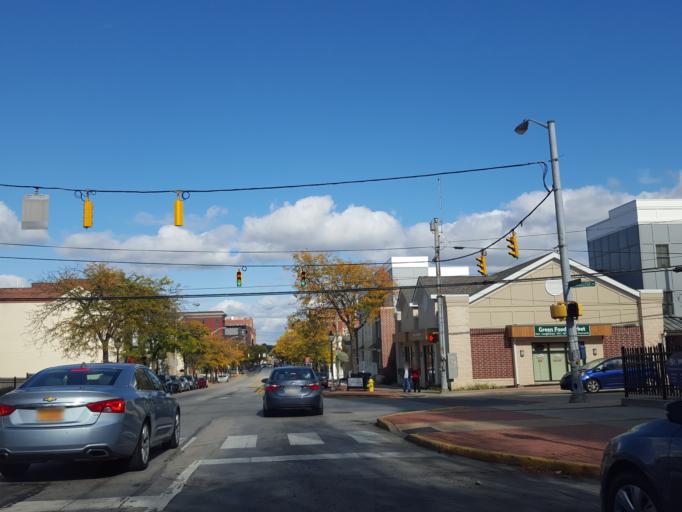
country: US
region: Pennsylvania
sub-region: York County
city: York
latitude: 39.9581
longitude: -76.7254
